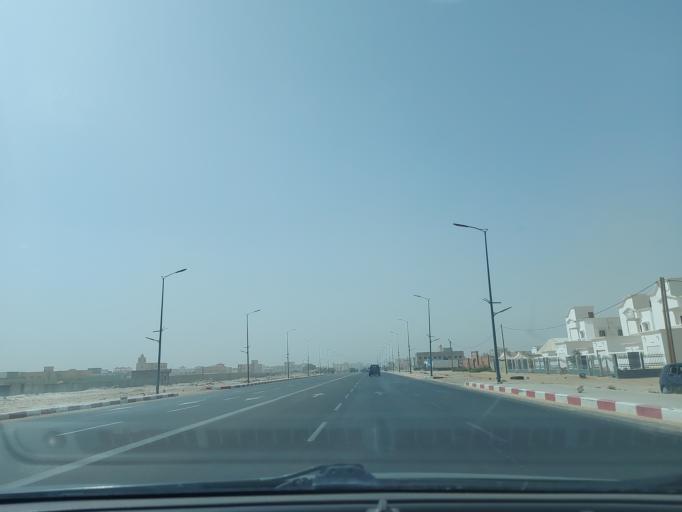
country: MR
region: Nouakchott
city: Nouakchott
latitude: 18.1335
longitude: -16.0044
